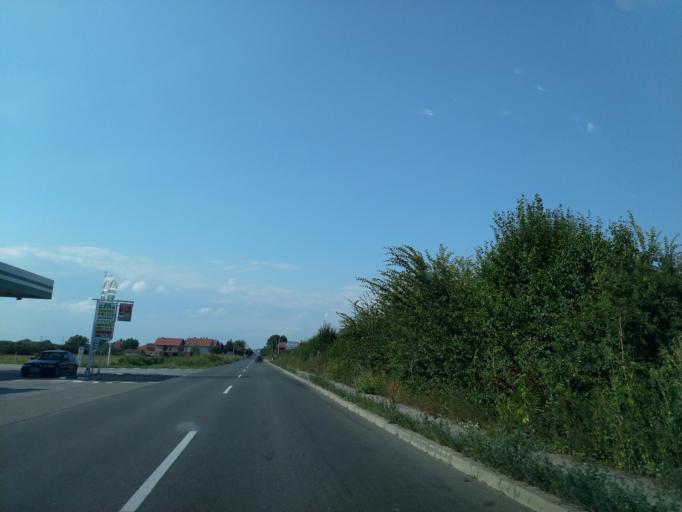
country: RS
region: Central Serbia
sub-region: Pomoravski Okrug
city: Paracin
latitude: 43.8260
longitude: 21.4177
